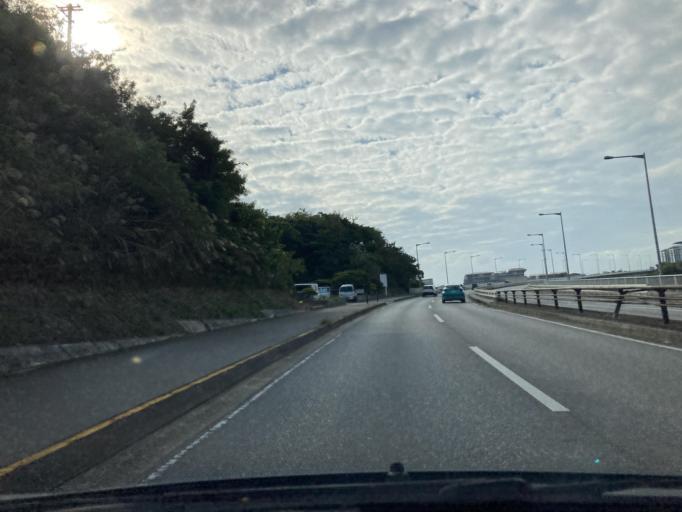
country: JP
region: Okinawa
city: Okinawa
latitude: 26.3146
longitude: 127.8072
